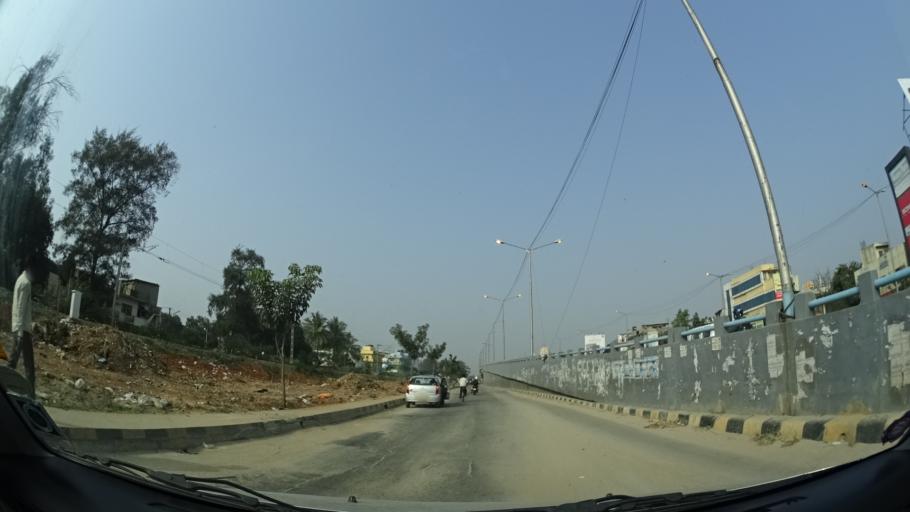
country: IN
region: Karnataka
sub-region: Bangalore Urban
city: Yelahanka
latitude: 13.0472
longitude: 77.5787
